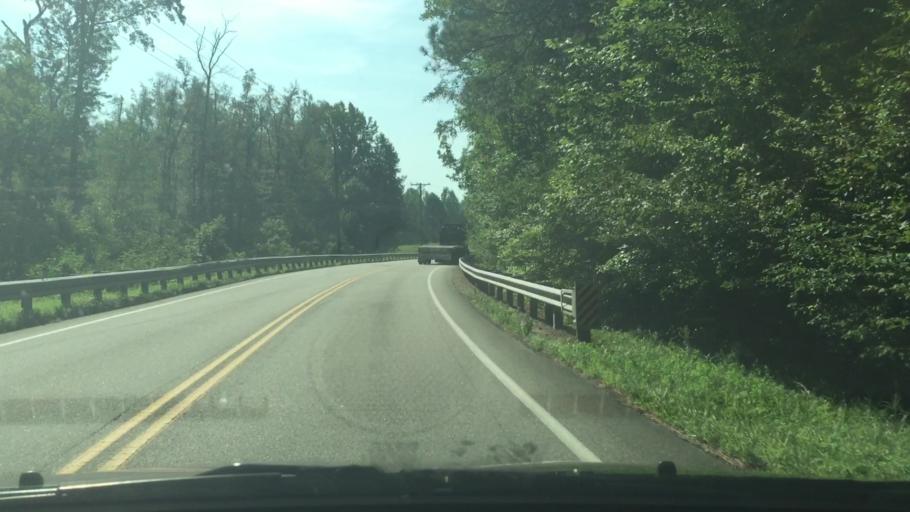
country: US
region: Virginia
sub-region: Sussex County
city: Sussex
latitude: 37.0482
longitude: -77.3152
